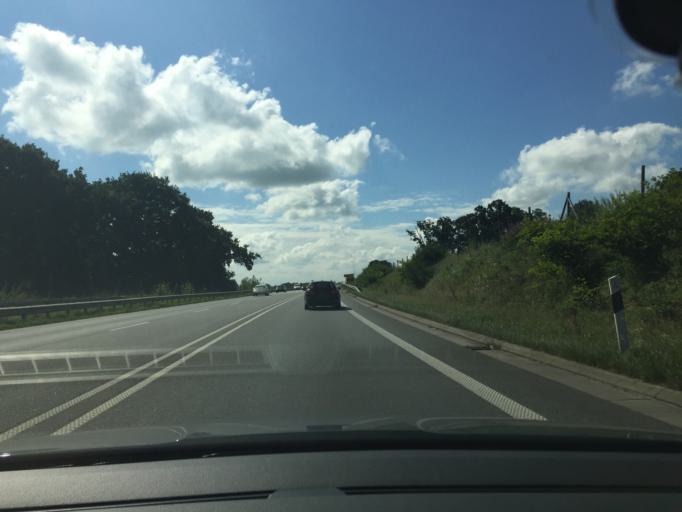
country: DE
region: Lower Saxony
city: Schortens
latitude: 53.5476
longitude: 7.9656
